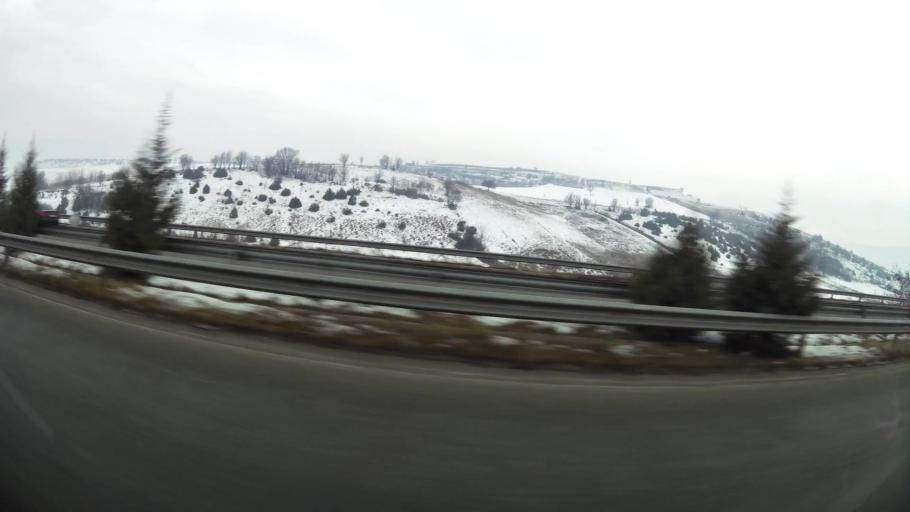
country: MK
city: Kondovo
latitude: 42.0190
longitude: 21.3314
